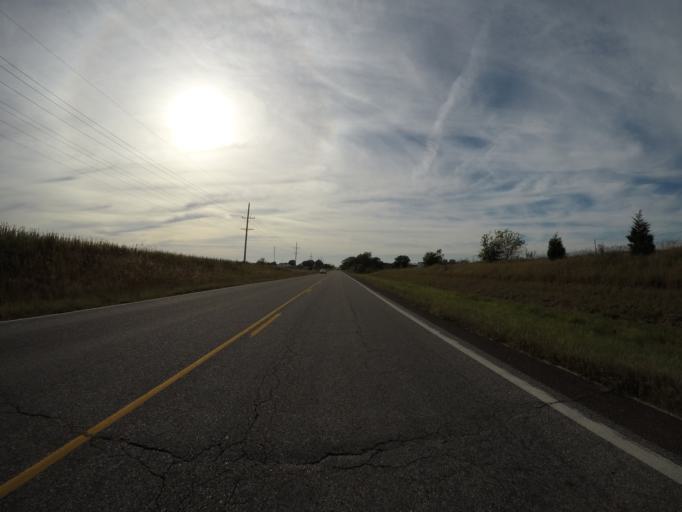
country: US
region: Kansas
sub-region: Franklin County
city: Wellsville
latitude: 38.7679
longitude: -95.0948
